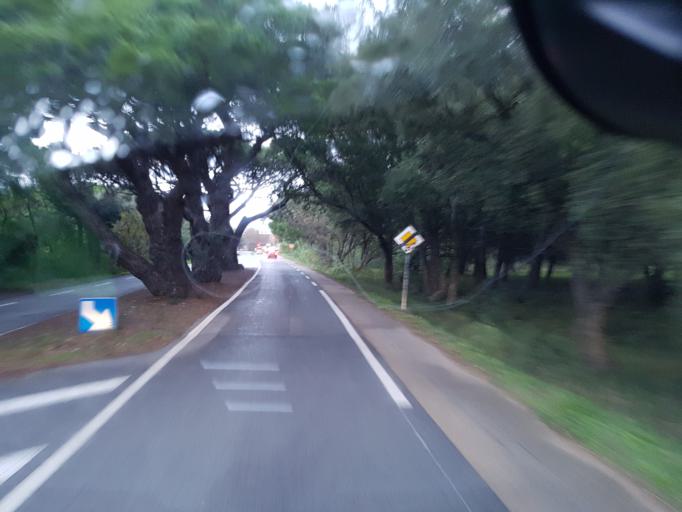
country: FR
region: Provence-Alpes-Cote d'Azur
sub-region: Departement du Var
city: Gassin
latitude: 43.2586
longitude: 6.5755
